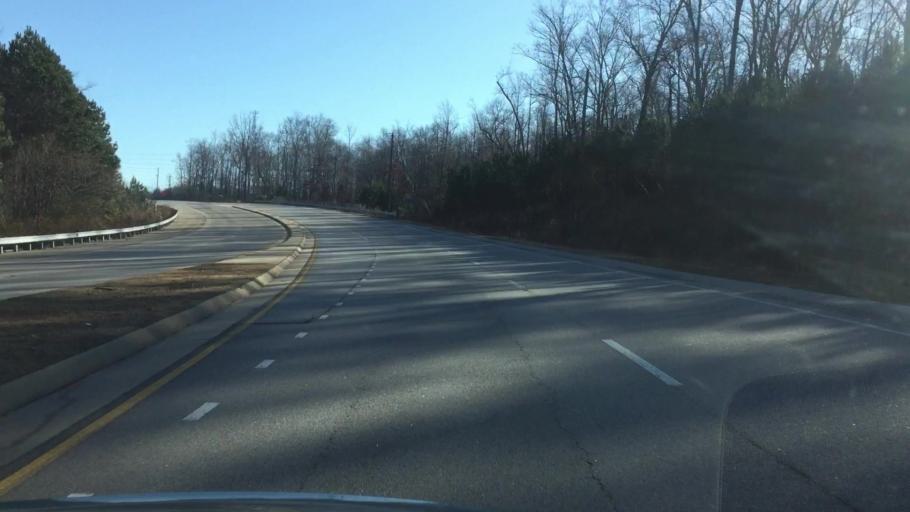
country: US
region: Georgia
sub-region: Henry County
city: McDonough
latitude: 33.5070
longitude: -84.1488
